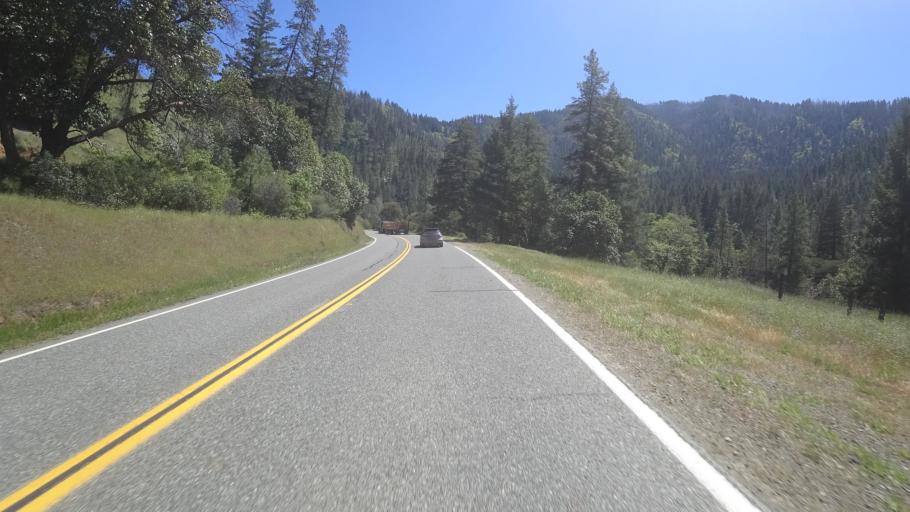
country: US
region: California
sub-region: Trinity County
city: Hayfork
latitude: 40.7747
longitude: -123.3323
